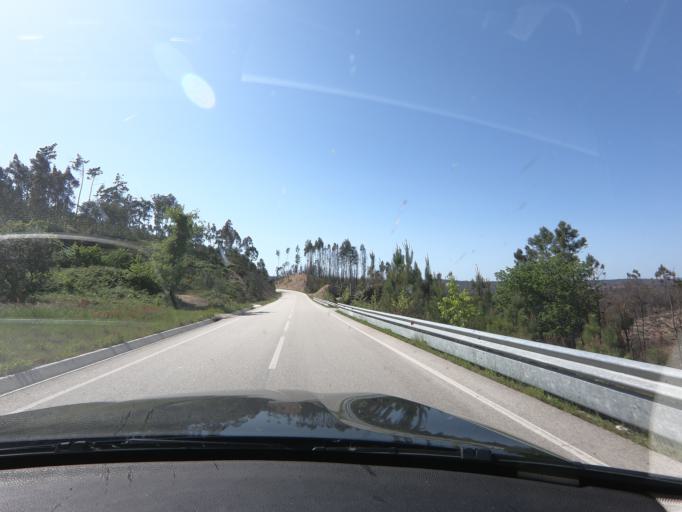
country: PT
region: Coimbra
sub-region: Penacova
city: Penacova
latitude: 40.2889
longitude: -8.2422
